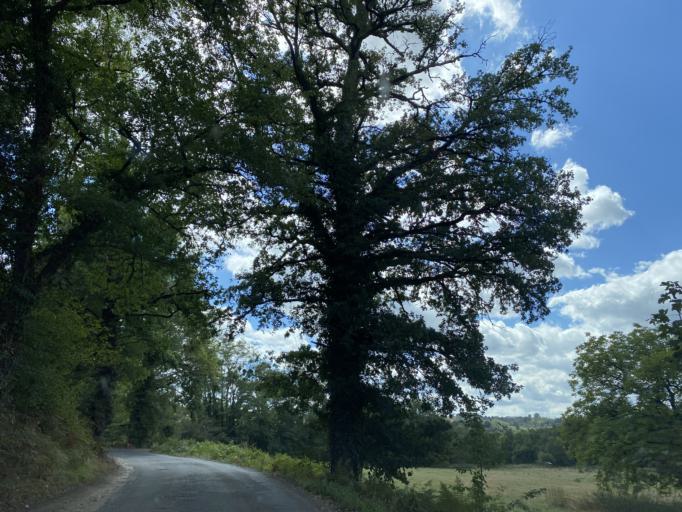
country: FR
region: Auvergne
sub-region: Departement du Puy-de-Dome
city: Courpiere
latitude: 45.7511
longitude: 3.5522
